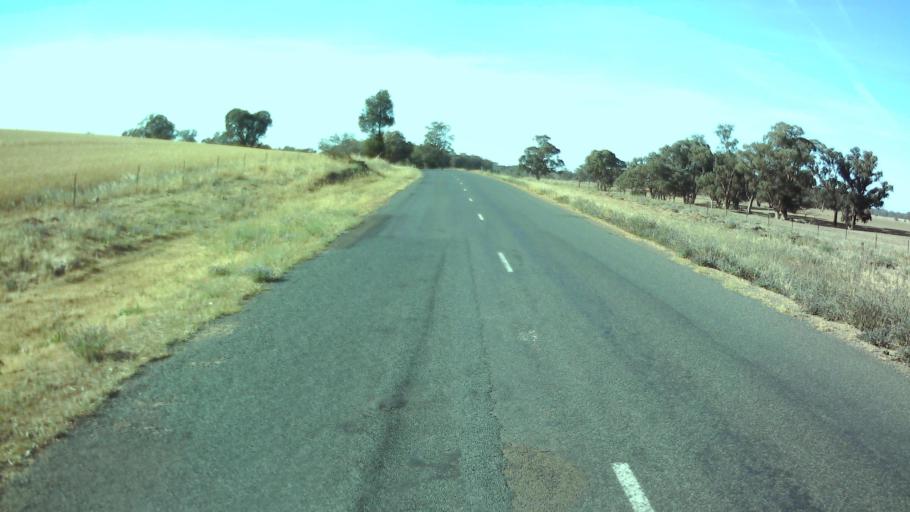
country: AU
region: New South Wales
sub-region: Weddin
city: Grenfell
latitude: -33.9707
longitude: 148.1408
